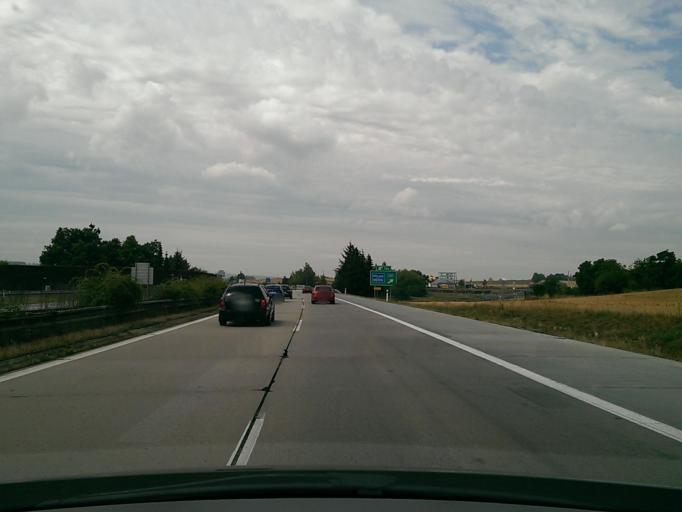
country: CZ
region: Vysocina
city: Merin
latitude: 49.3965
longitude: 15.8867
